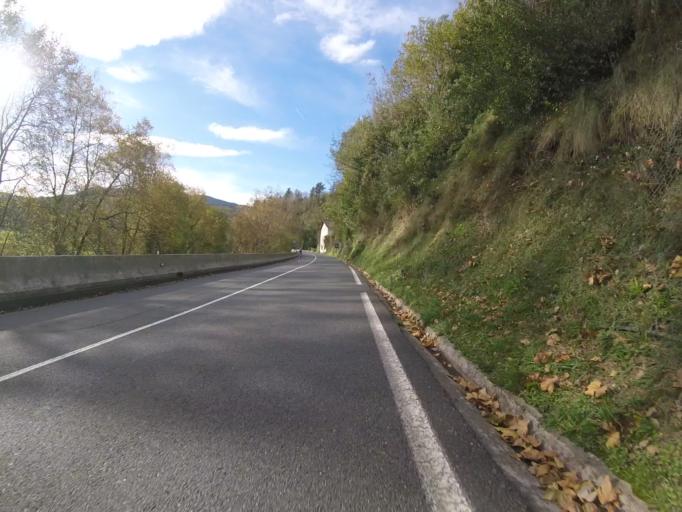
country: ES
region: Basque Country
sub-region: Provincia de Guipuzcoa
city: Usurbil
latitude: 43.2779
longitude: -2.0660
